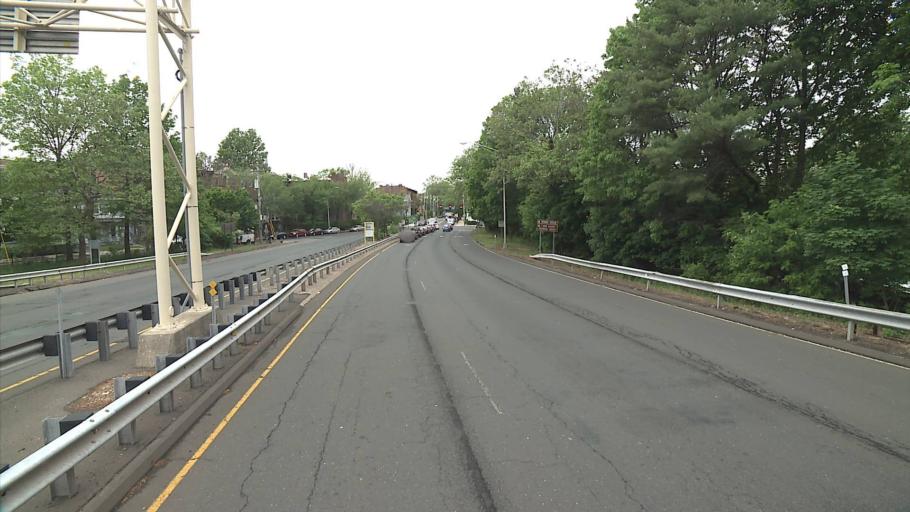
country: US
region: Connecticut
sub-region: New Haven County
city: New Haven
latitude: 41.3117
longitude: -72.9178
